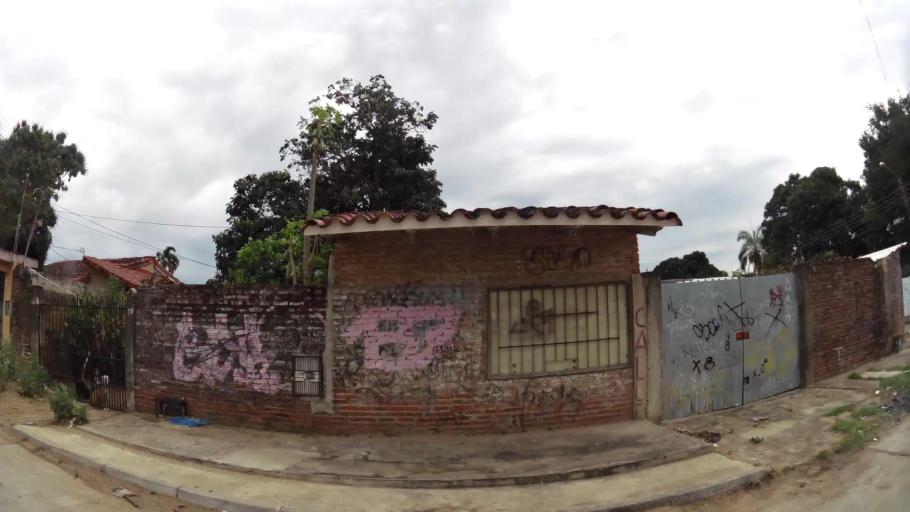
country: BO
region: Santa Cruz
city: Santa Cruz de la Sierra
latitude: -17.7442
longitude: -63.1922
